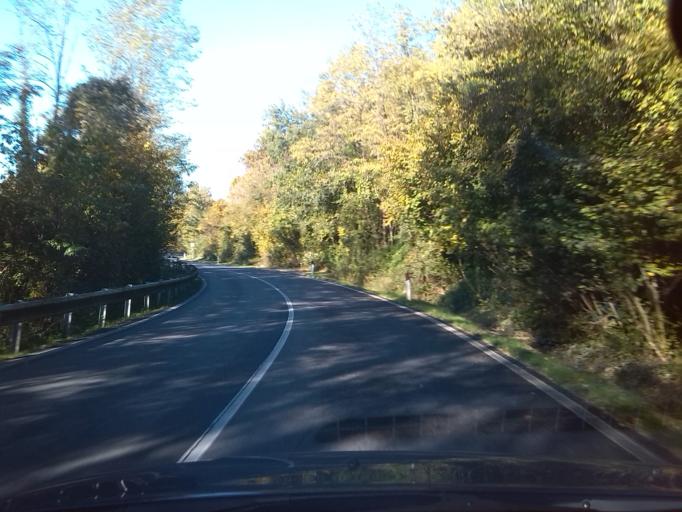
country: IT
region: Friuli Venezia Giulia
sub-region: Provincia di Udine
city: Corno di Rosazzo
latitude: 45.9972
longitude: 13.4688
